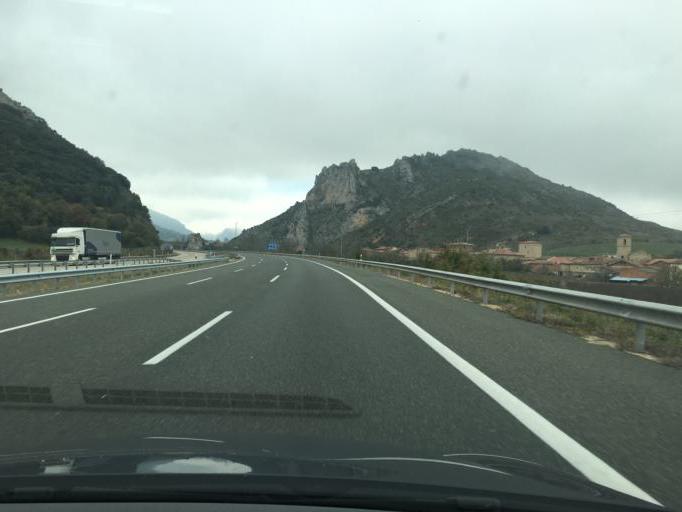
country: ES
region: Castille and Leon
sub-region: Provincia de Burgos
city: Ameyugo
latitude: 42.6554
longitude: -3.0570
